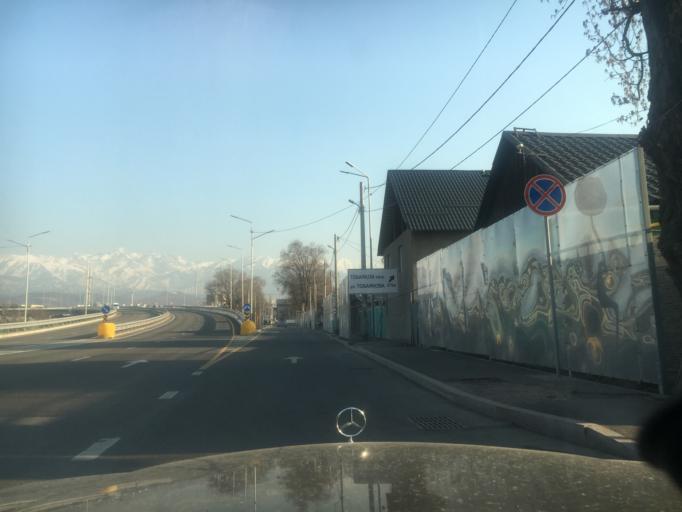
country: KZ
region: Almaty Qalasy
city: Almaty
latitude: 43.2793
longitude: 76.9403
